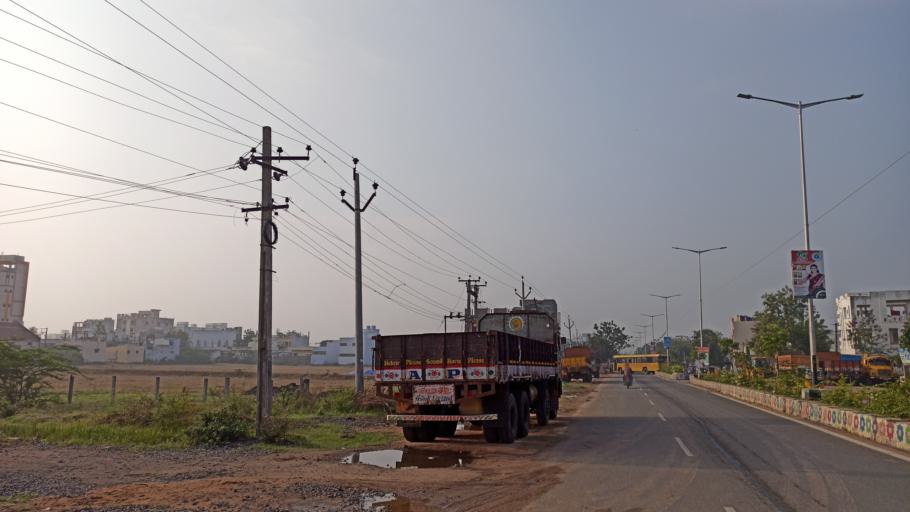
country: IN
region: Andhra Pradesh
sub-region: Guntur
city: Narasaraopet
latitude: 16.2523
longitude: 80.0577
